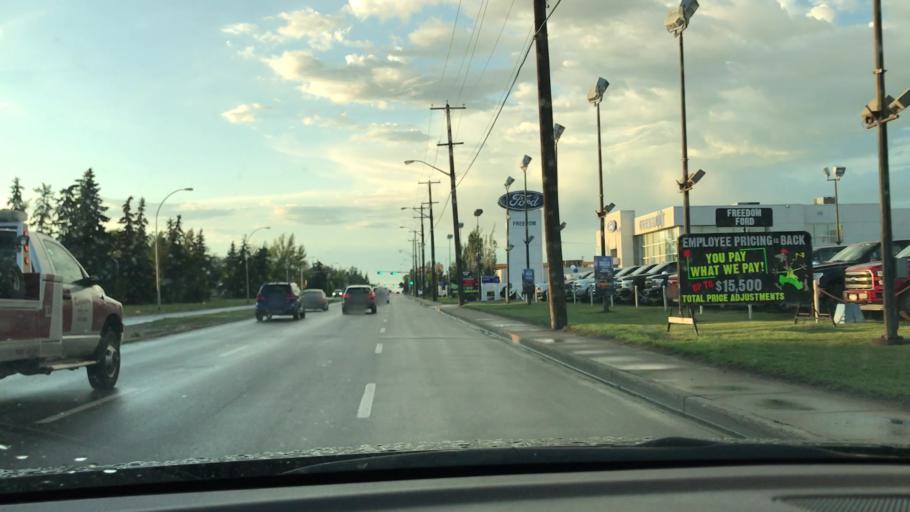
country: CA
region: Alberta
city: Edmonton
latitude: 53.5103
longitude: -113.4427
